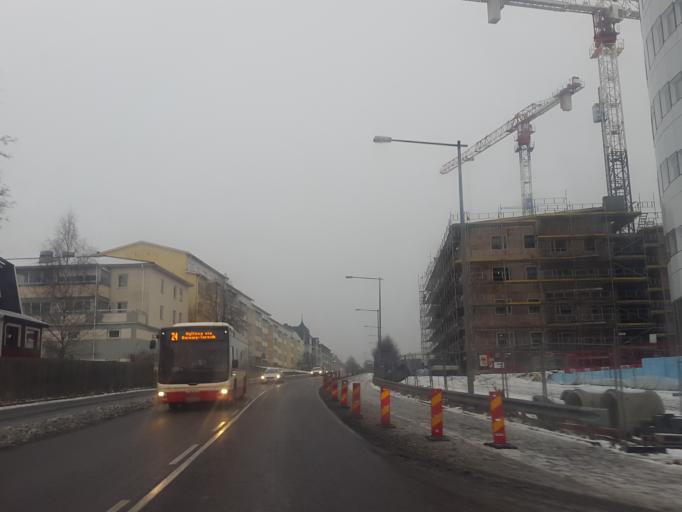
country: SE
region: Joenkoeping
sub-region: Jonkopings Kommun
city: Jonkoping
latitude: 57.7684
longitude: 14.1540
